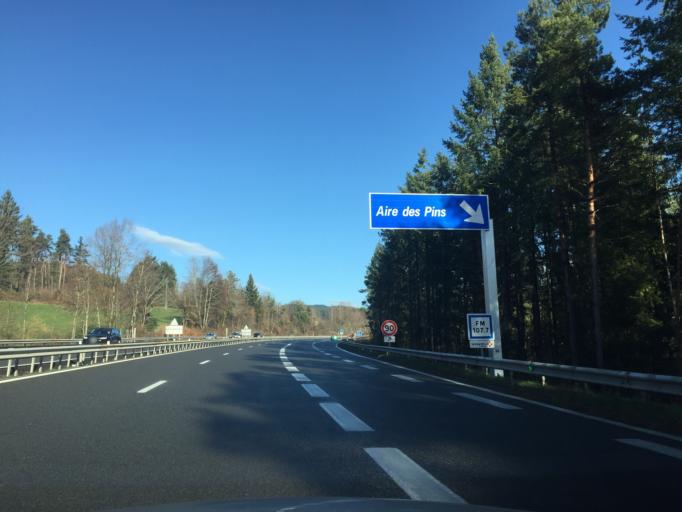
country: FR
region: Auvergne
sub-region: Departement du Puy-de-Dome
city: Saint-Remy-sur-Durolle
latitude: 45.8787
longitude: 3.5677
